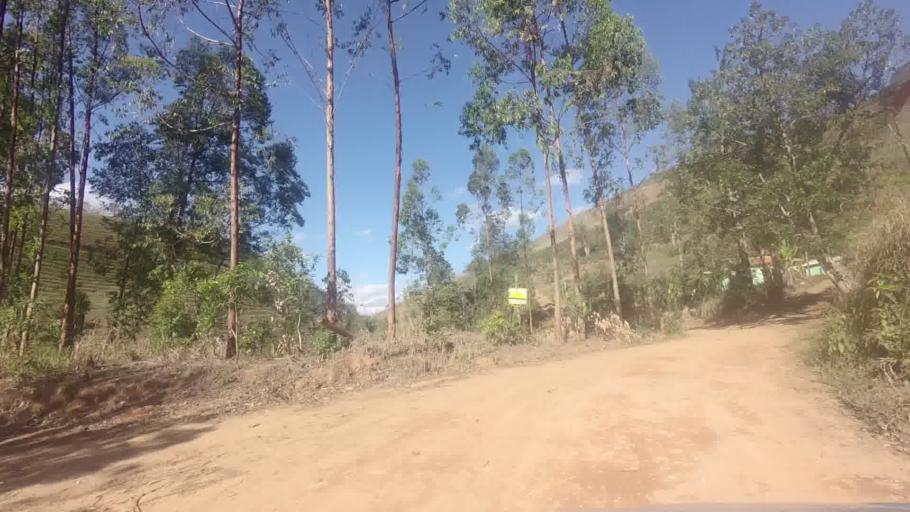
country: BR
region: Espirito Santo
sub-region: Sao Jose Do Calcado
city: Sao Jose do Calcado
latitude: -21.0255
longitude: -41.5743
